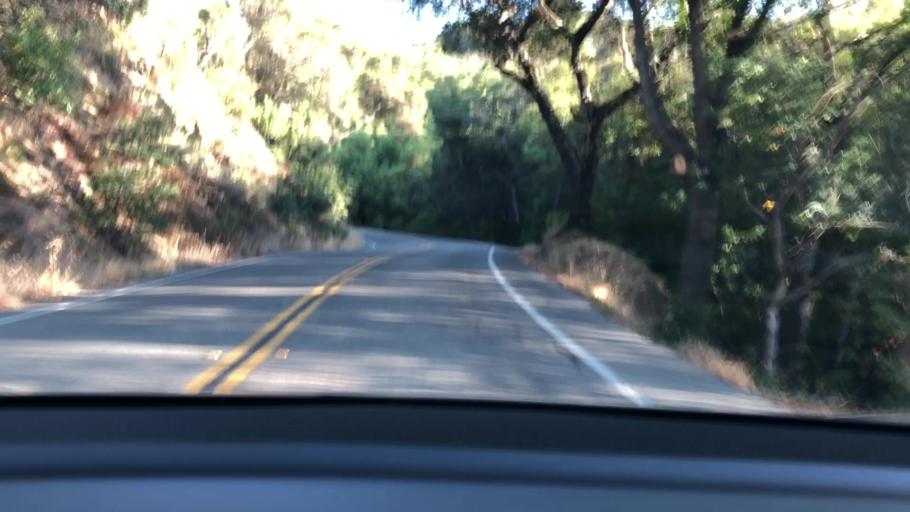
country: US
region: California
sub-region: Santa Clara County
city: Saratoga
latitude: 37.2787
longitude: -122.0720
